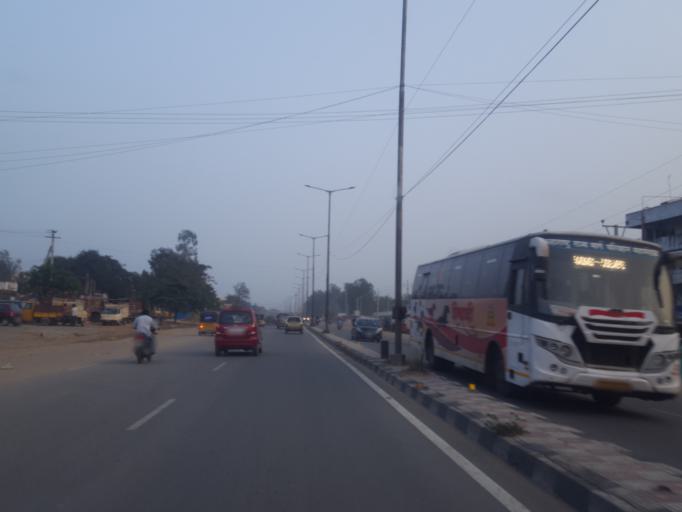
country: IN
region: Telangana
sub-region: Medak
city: Patancheru
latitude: 17.5281
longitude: 78.2676
